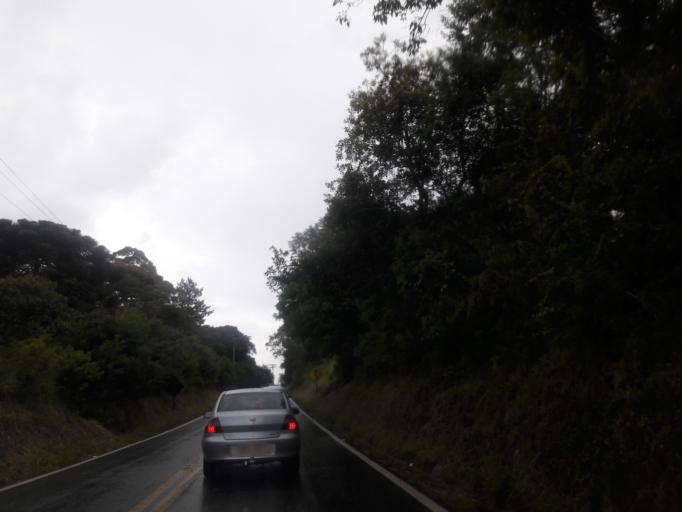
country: BR
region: Sao Paulo
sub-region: Aruja
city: Aruja
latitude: -23.3261
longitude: -46.4324
